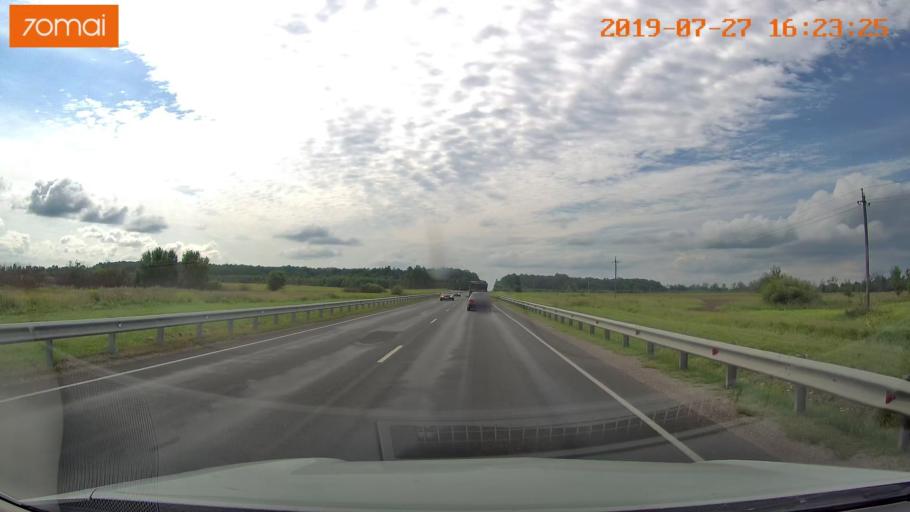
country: RU
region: Kaliningrad
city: Zheleznodorozhnyy
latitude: 54.6310
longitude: 21.4744
